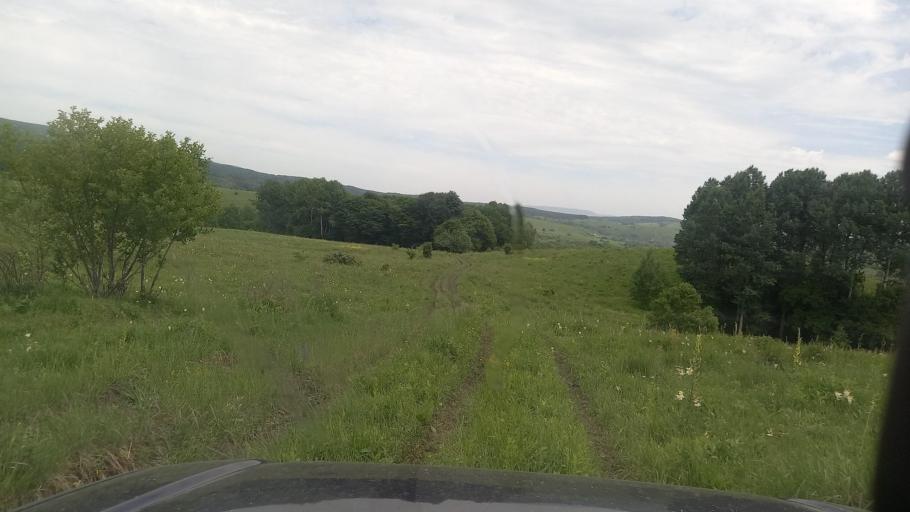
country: RU
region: Karachayevo-Cherkesiya
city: Pregradnaya
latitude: 44.0810
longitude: 41.2318
